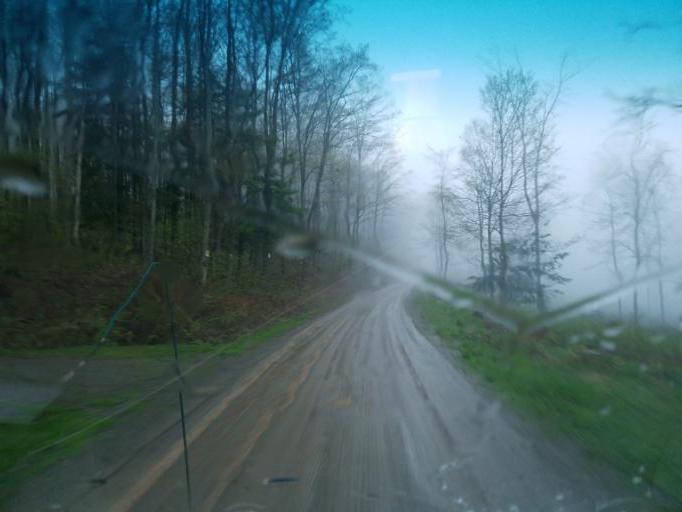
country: US
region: Pennsylvania
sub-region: Tioga County
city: Westfield
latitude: 41.9327
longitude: -77.7048
